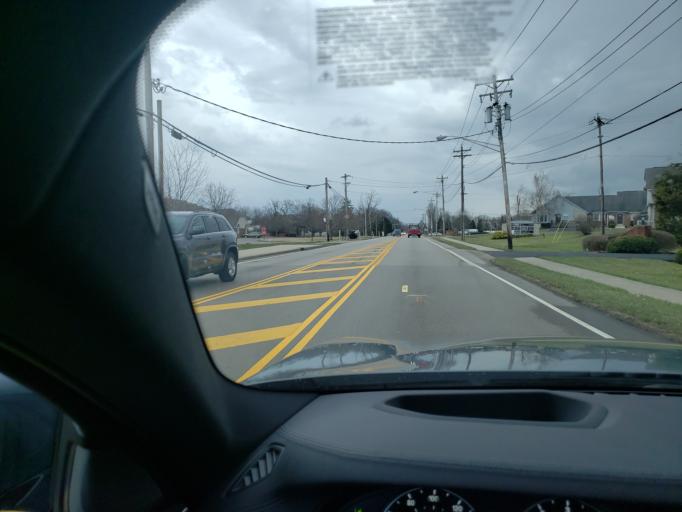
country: US
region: Ohio
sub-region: Hamilton County
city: Springdale
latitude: 39.2803
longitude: -84.4844
